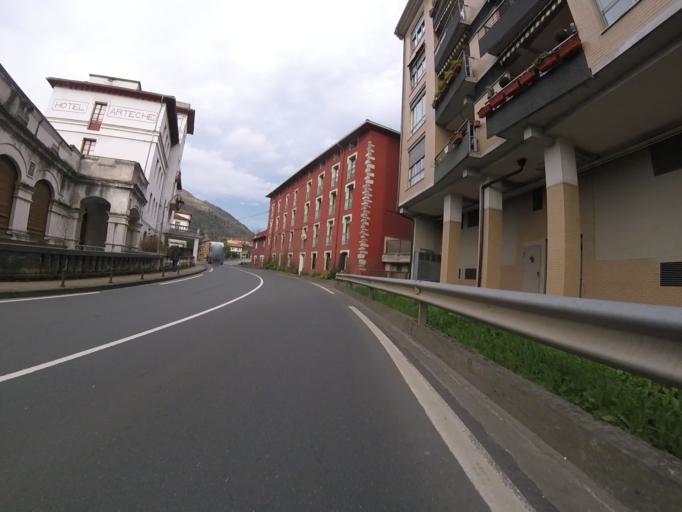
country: ES
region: Basque Country
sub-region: Provincia de Guipuzcoa
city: Cestona
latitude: 43.2375
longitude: -2.2545
